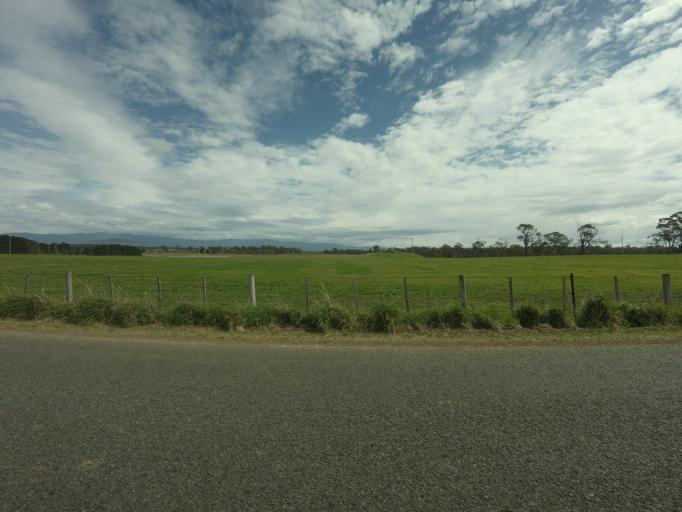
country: AU
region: Tasmania
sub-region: Northern Midlands
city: Longford
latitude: -41.7453
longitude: 147.2038
